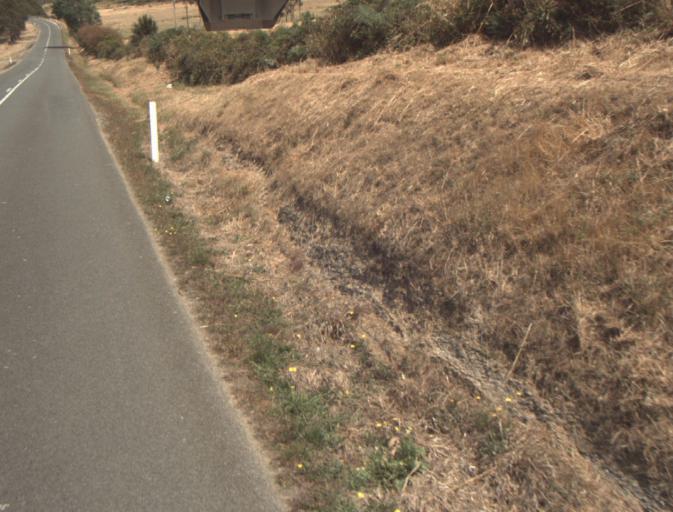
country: AU
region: Tasmania
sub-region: Launceston
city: Mayfield
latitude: -41.2203
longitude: 147.1215
